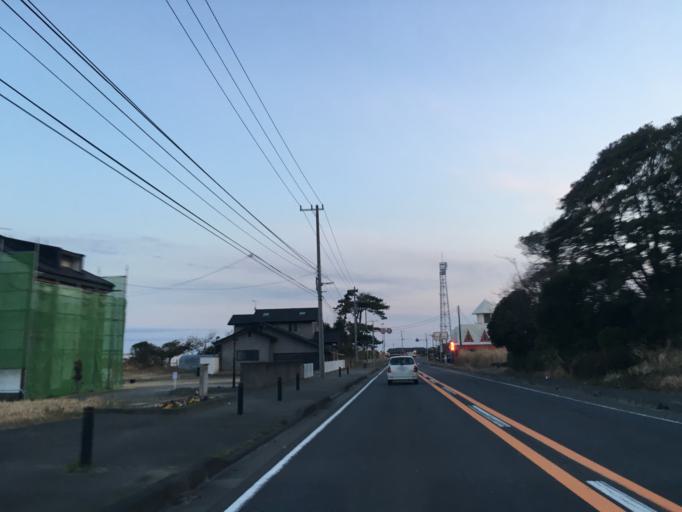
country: JP
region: Ibaraki
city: Kitaibaraki
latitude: 36.7611
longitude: 140.7369
